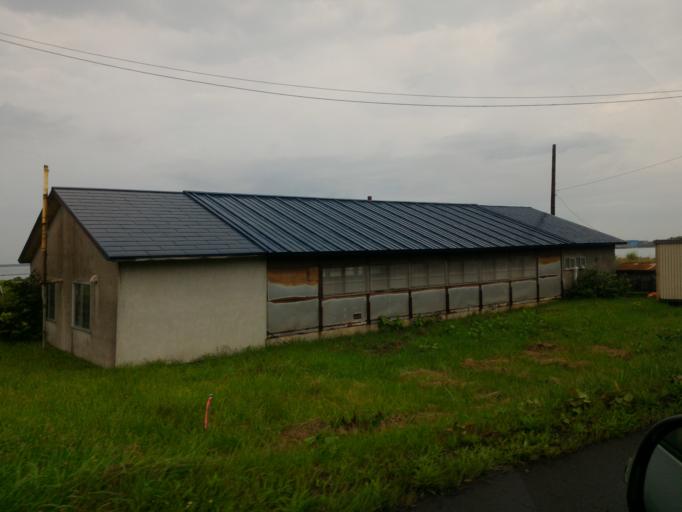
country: JP
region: Hokkaido
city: Rumoi
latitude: 43.9629
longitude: 141.6432
